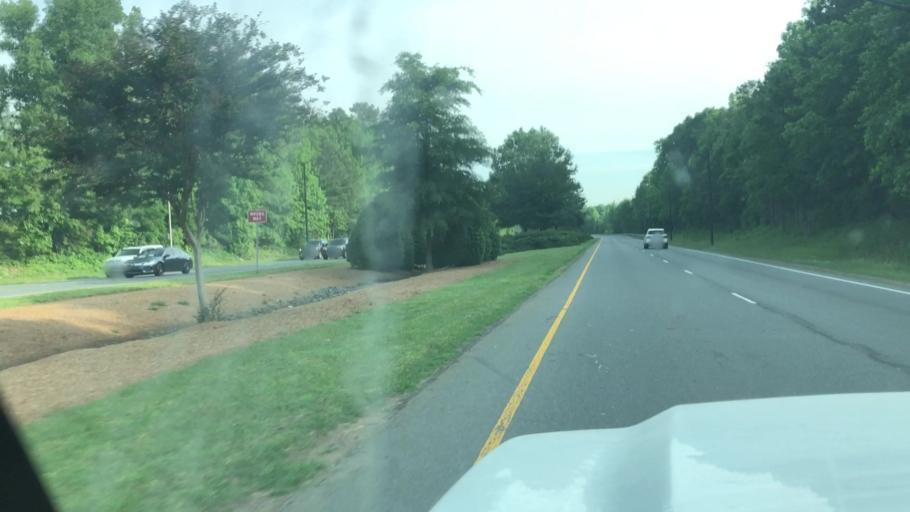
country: US
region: North Carolina
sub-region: Gaston County
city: Mount Holly
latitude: 35.3012
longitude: -80.9204
